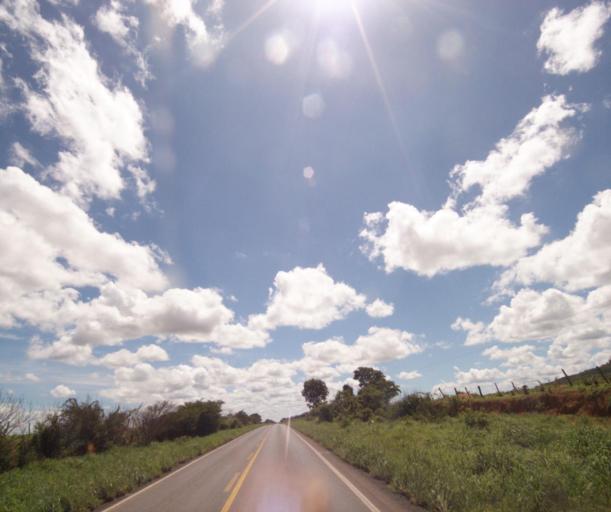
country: BR
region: Bahia
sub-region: Sao Felix Do Coribe
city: Santa Maria da Vitoria
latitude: -13.3920
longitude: -44.1174
